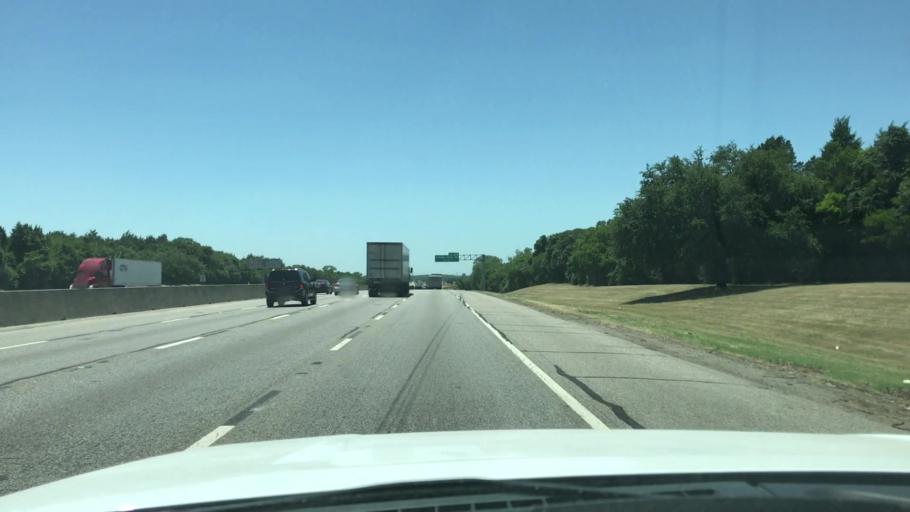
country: US
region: Texas
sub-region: Dallas County
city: Hutchins
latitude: 32.6818
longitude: -96.6634
